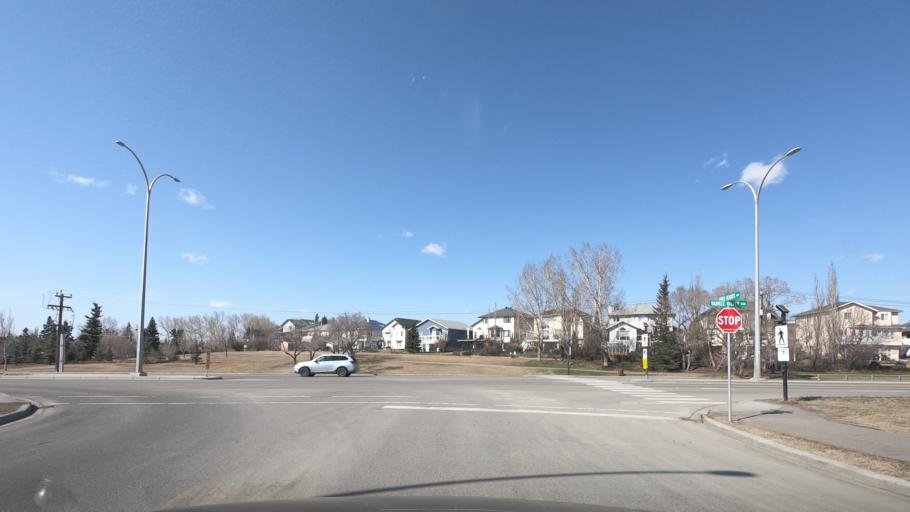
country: CA
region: Alberta
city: Airdrie
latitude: 51.2705
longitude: -113.9816
